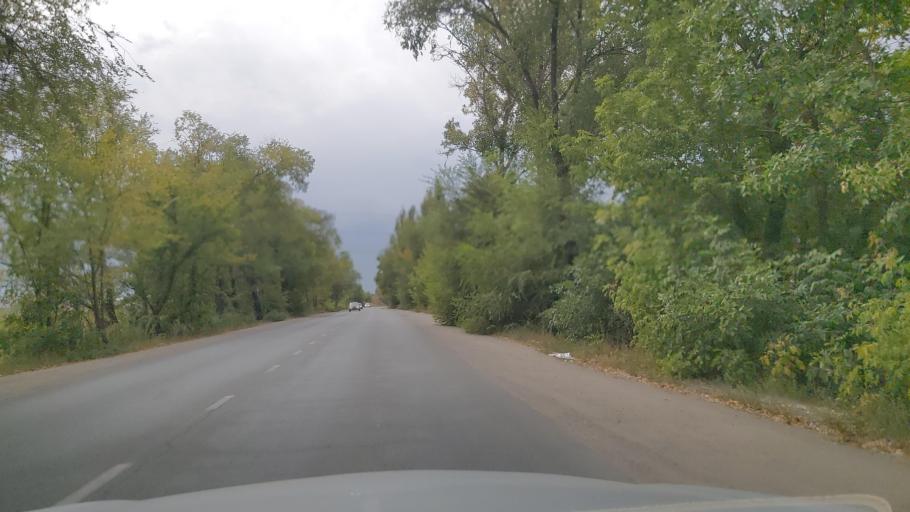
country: KZ
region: Almaty Oblysy
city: Energeticheskiy
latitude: 43.4031
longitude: 77.0366
